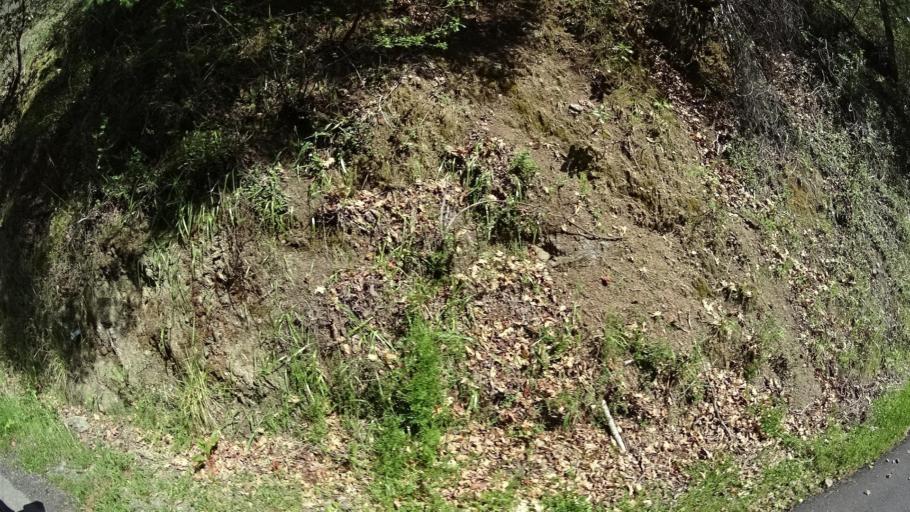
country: US
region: California
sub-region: Humboldt County
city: Redway
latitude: 40.3143
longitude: -123.6594
